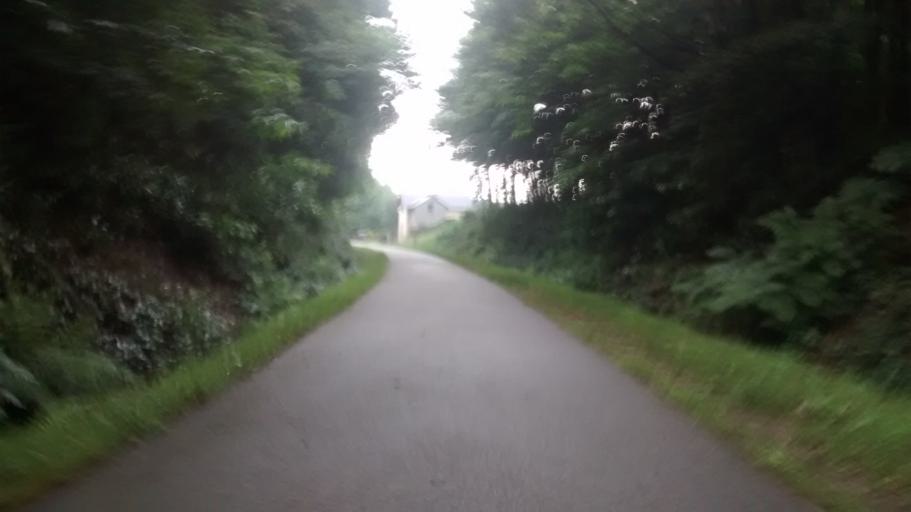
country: FR
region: Brittany
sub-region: Departement du Morbihan
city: Pleucadeuc
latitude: 47.7703
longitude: -2.3951
